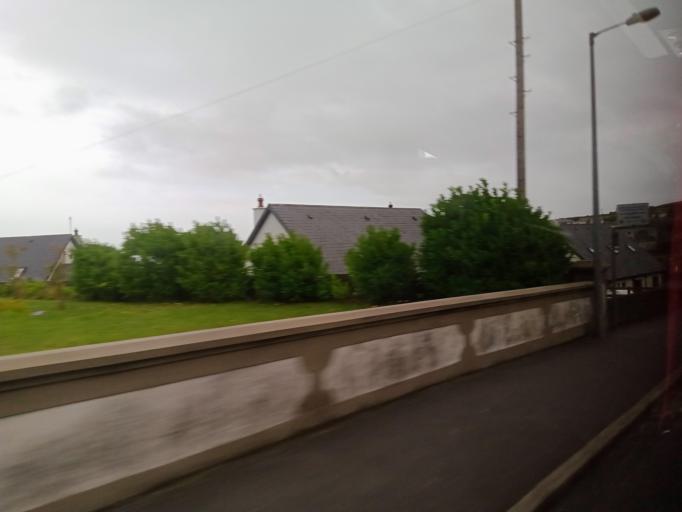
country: IE
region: Munster
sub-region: Waterford
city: Dungarvan
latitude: 52.0465
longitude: -7.5707
